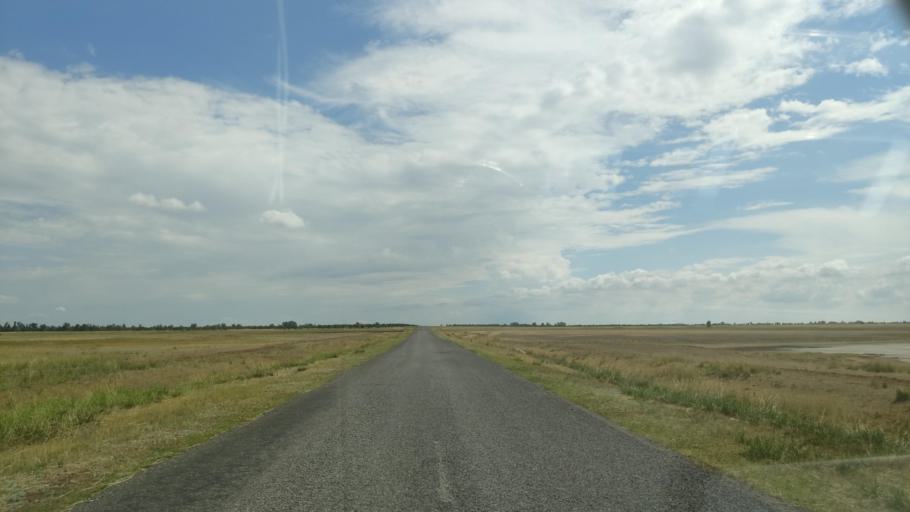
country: KZ
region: Pavlodar
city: Pavlodar
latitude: 52.6361
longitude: 76.9450
